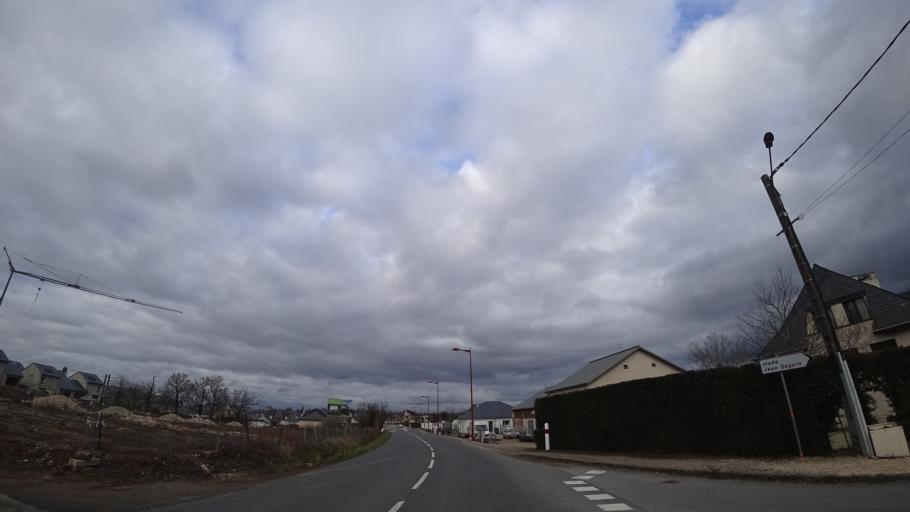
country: FR
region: Midi-Pyrenees
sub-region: Departement de l'Aveyron
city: Le Monastere
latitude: 44.3336
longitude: 2.5734
